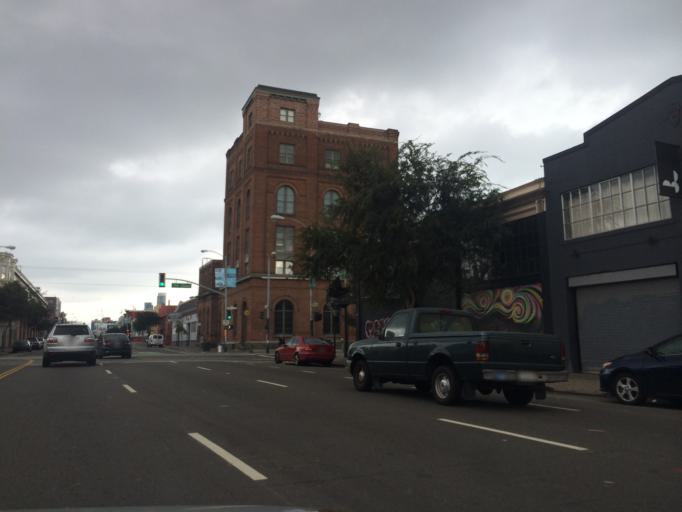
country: US
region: California
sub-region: San Francisco County
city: San Francisco
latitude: 37.7716
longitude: -122.4145
